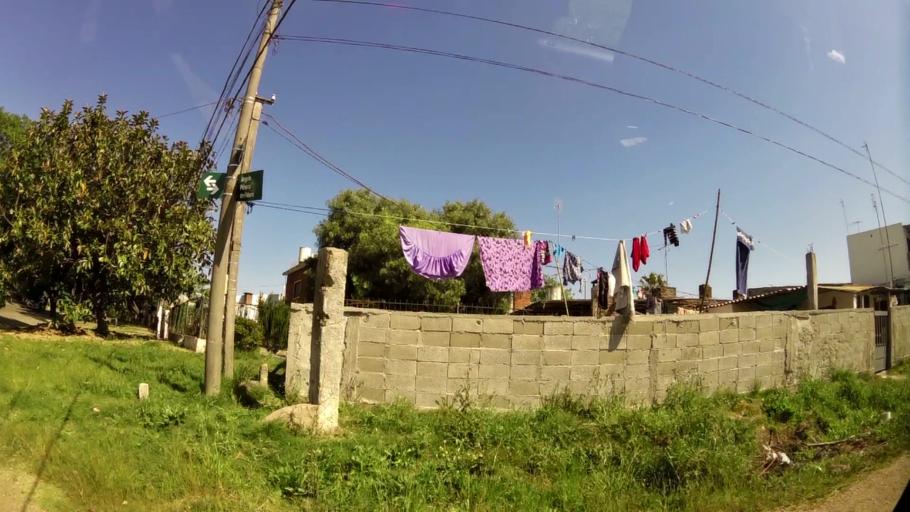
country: UY
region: Canelones
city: La Paz
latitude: -34.8358
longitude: -56.2575
